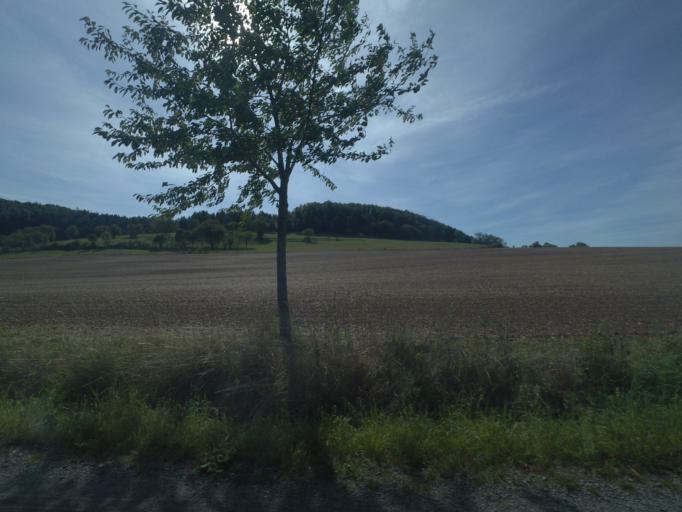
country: DE
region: Thuringia
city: Metzels
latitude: 50.6455
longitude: 10.4505
